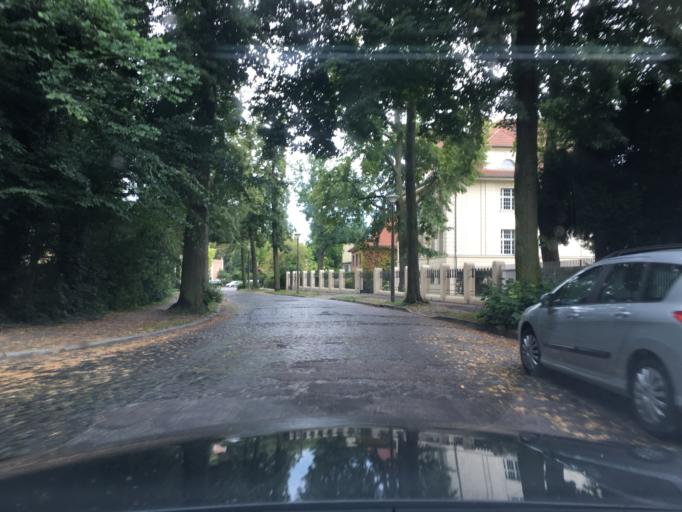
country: DE
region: Brandenburg
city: Potsdam
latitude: 52.4099
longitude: 13.0727
